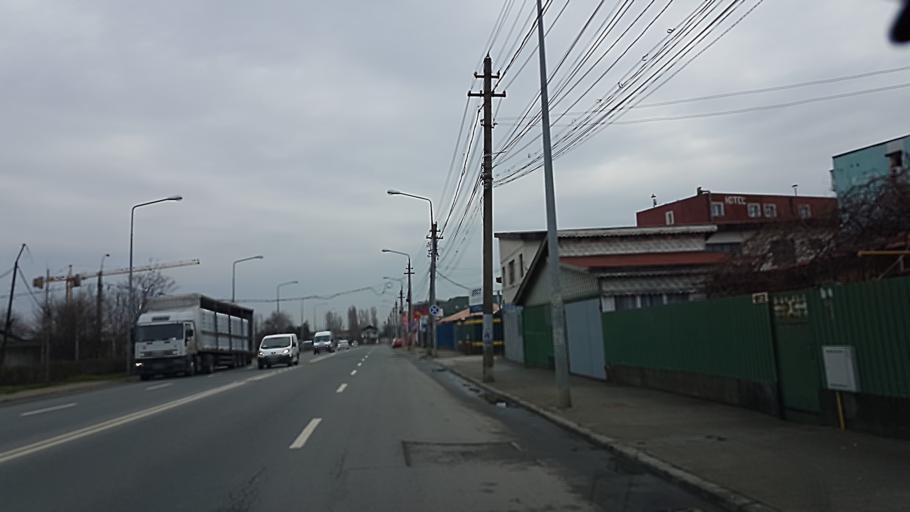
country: RO
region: Ilfov
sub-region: Comuna Glina
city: Catelu
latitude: 44.4278
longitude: 26.2179
